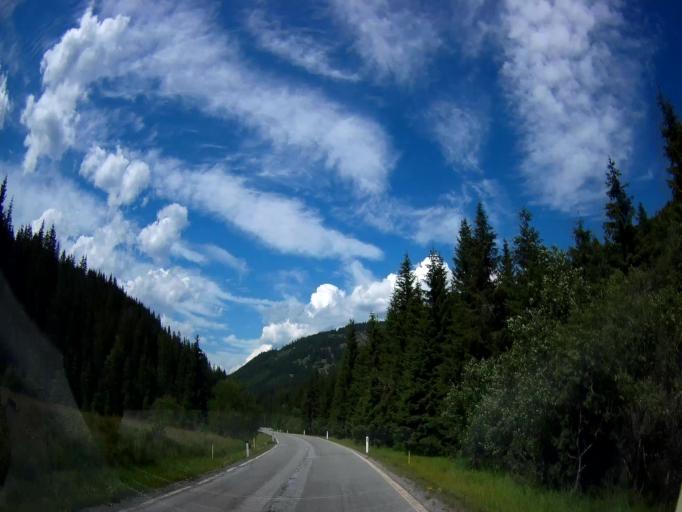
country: AT
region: Styria
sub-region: Politischer Bezirk Murau
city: Stadl an der Mur
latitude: 46.9937
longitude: 14.0150
